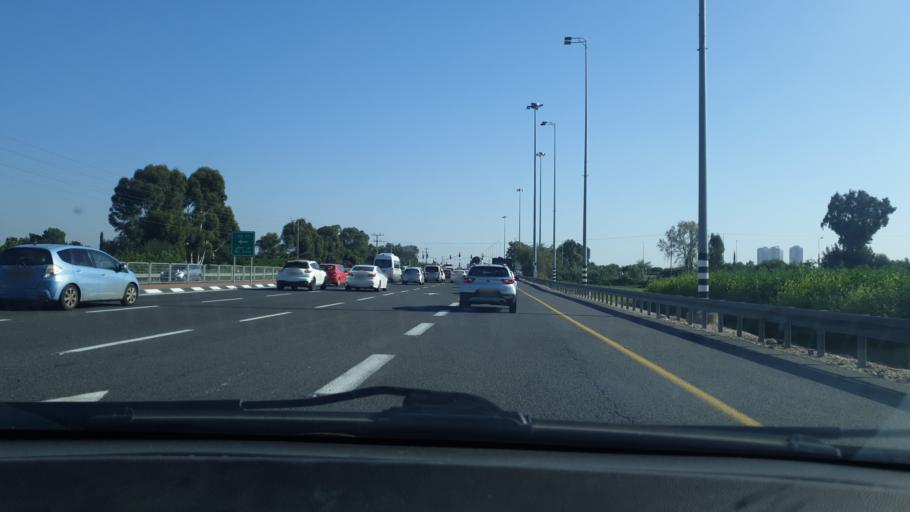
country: IL
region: Central District
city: Ramla
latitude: 31.9537
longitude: 34.8553
